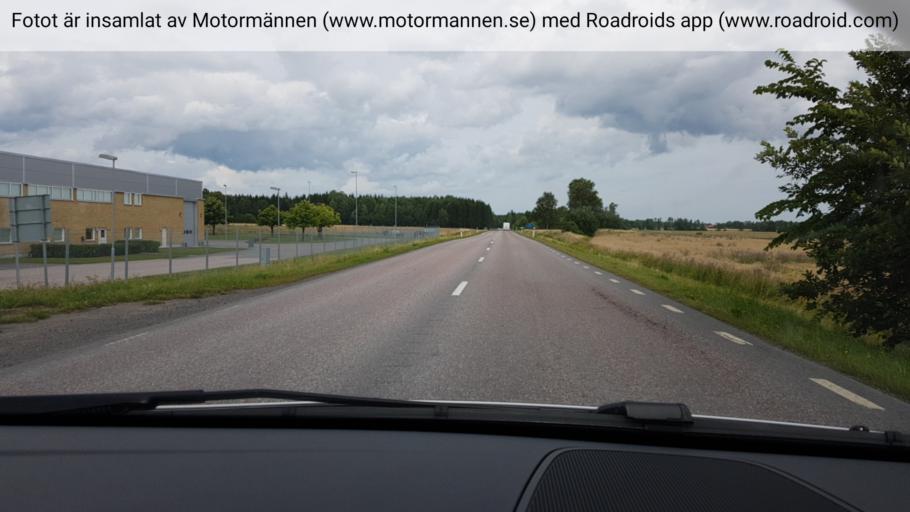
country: SE
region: Uppsala
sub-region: Osthammars Kommun
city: Gimo
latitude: 60.1812
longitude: 18.1904
